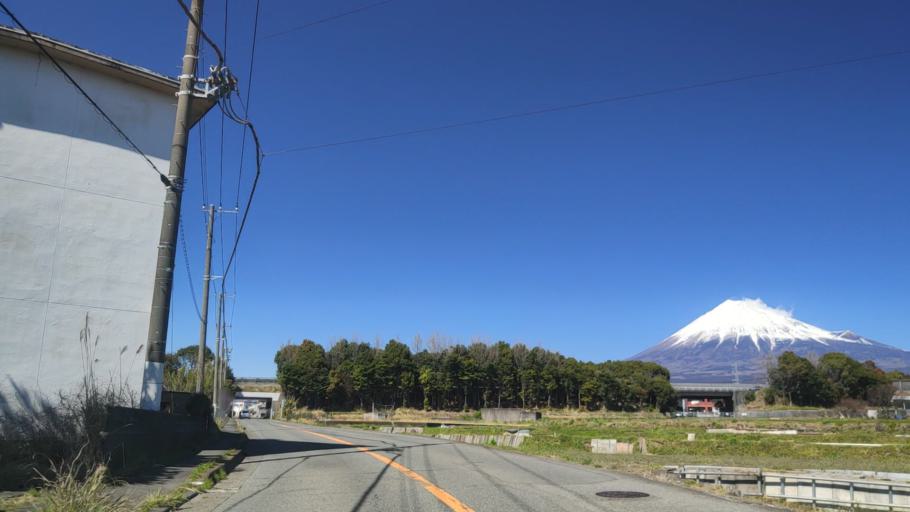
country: JP
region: Shizuoka
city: Fuji
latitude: 35.1756
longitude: 138.6570
